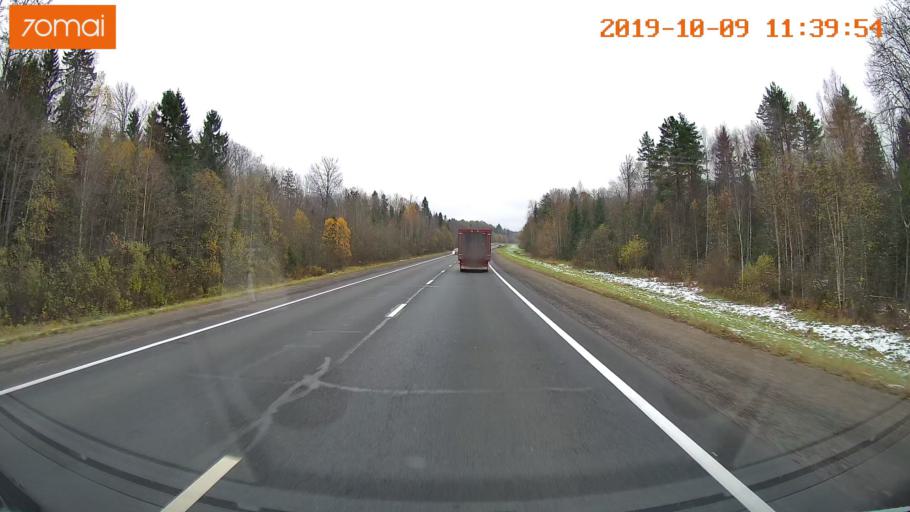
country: RU
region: Vologda
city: Gryazovets
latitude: 58.9504
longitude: 40.1706
